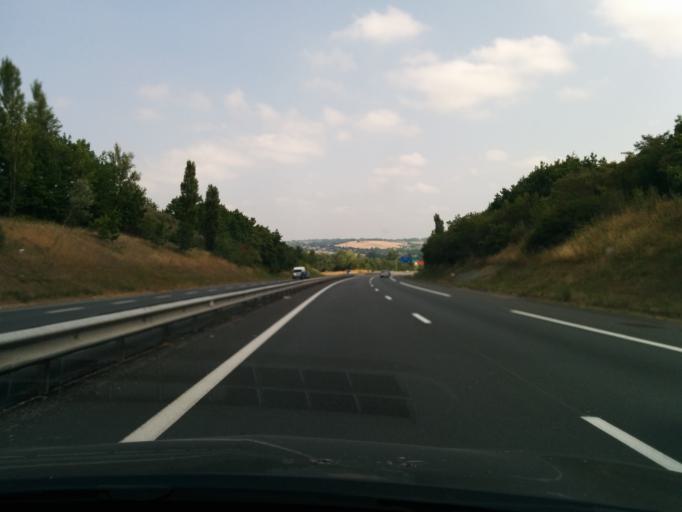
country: FR
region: Midi-Pyrenees
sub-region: Departement de la Haute-Garonne
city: Gragnague
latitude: 43.6806
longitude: 1.5613
